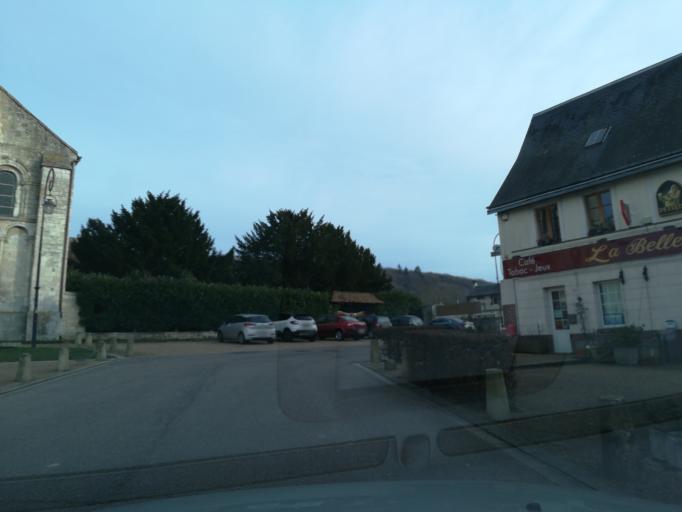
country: FR
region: Haute-Normandie
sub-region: Departement de la Seine-Maritime
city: Saint-Martin-de-Boscherville
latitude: 49.4444
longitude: 0.9636
